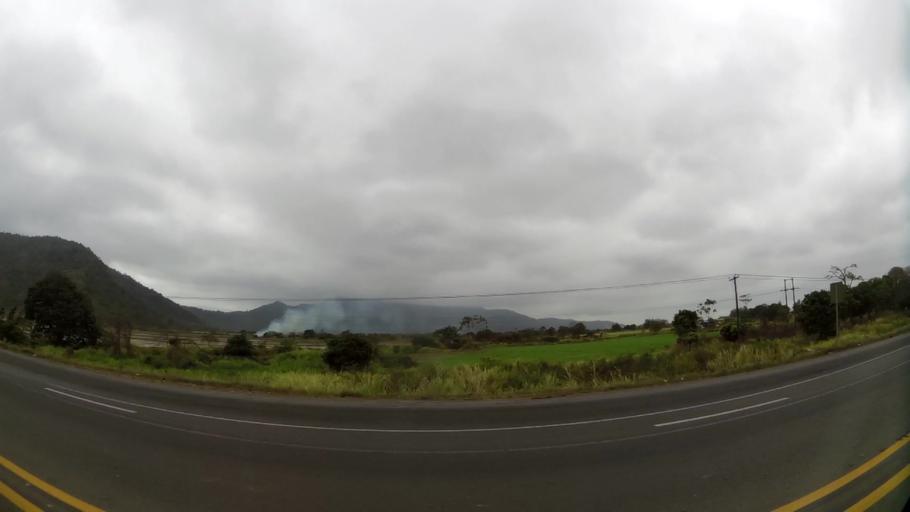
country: EC
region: Guayas
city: Naranjal
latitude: -2.4693
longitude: -79.6225
